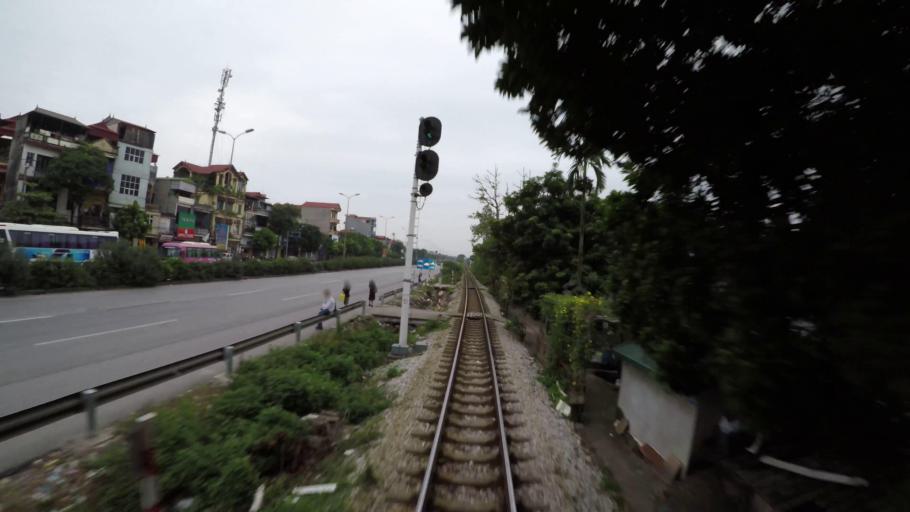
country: VN
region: Hung Yen
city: Nhu Quynh
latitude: 21.0015
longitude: 105.9650
